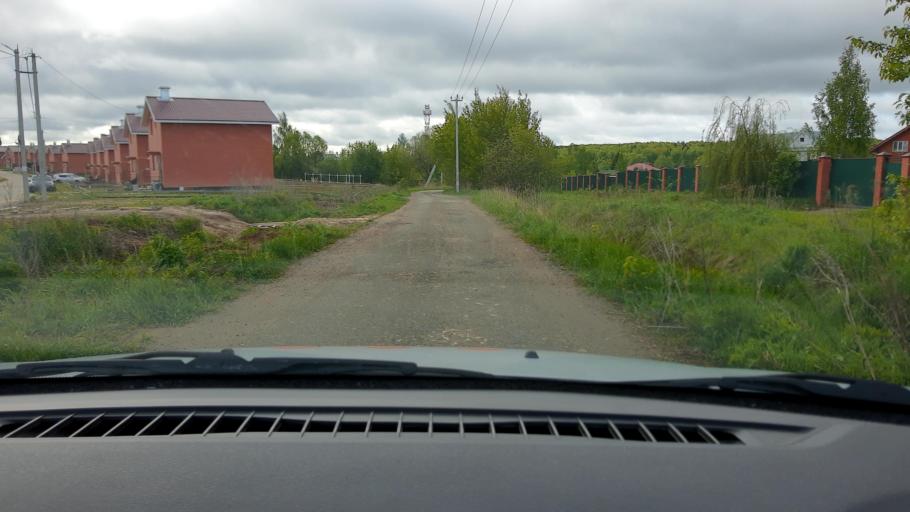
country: RU
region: Nizjnij Novgorod
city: Afonino
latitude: 56.1951
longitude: 44.0686
